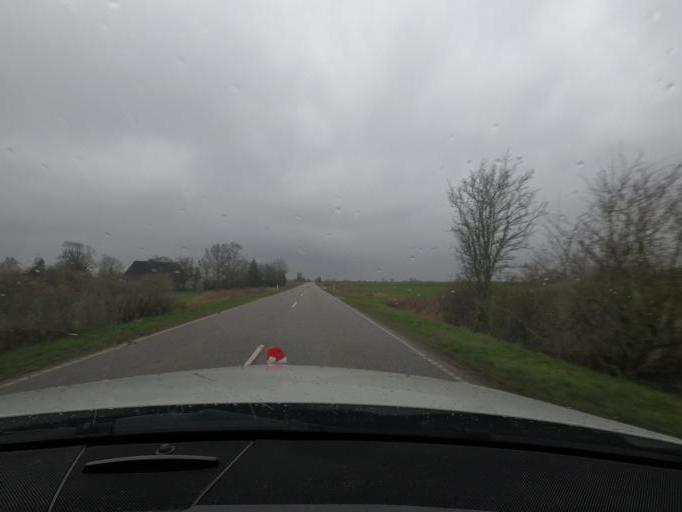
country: DK
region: South Denmark
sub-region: Haderslev Kommune
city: Starup
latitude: 55.2342
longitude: 9.6447
